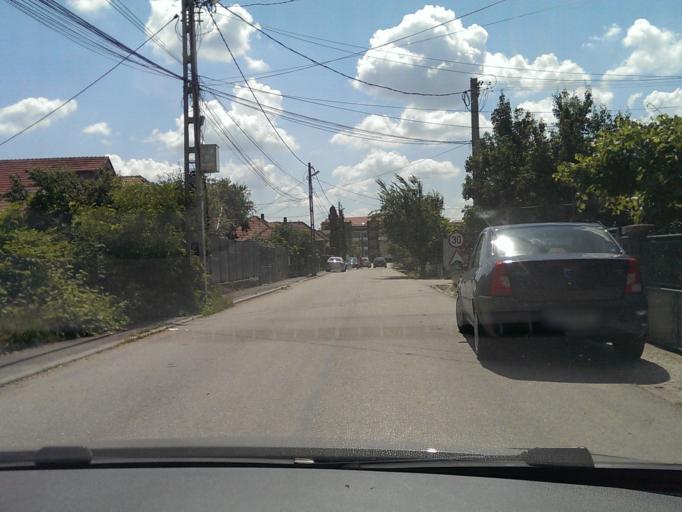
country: RO
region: Cluj
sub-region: Comuna Apahida
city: Apahida
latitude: 46.7962
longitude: 23.7474
